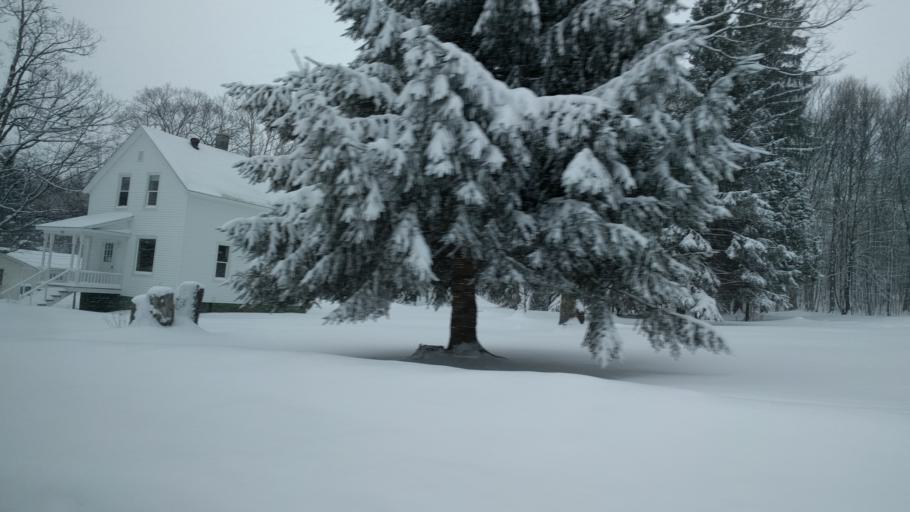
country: US
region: Wisconsin
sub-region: Iron County
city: Hurley
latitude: 46.4283
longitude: -90.2419
